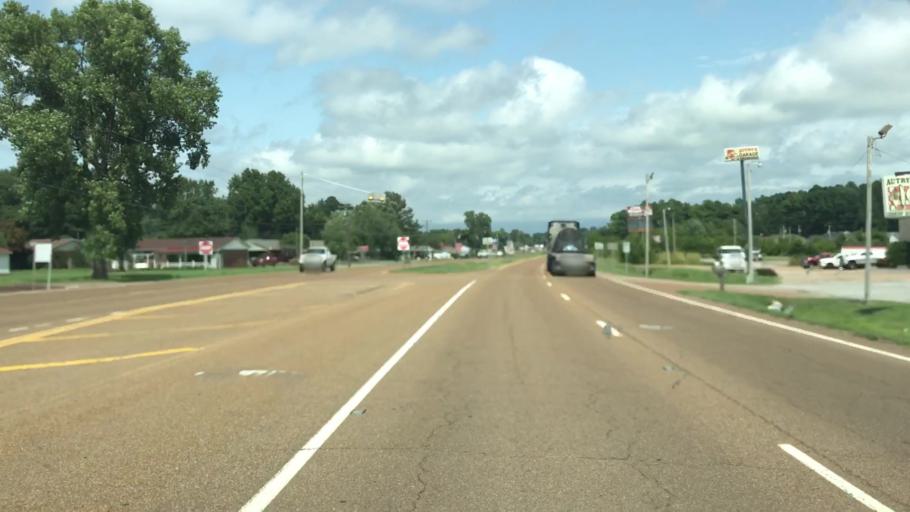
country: US
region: Tennessee
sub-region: Obion County
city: Troy
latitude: 36.3447
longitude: -89.1522
